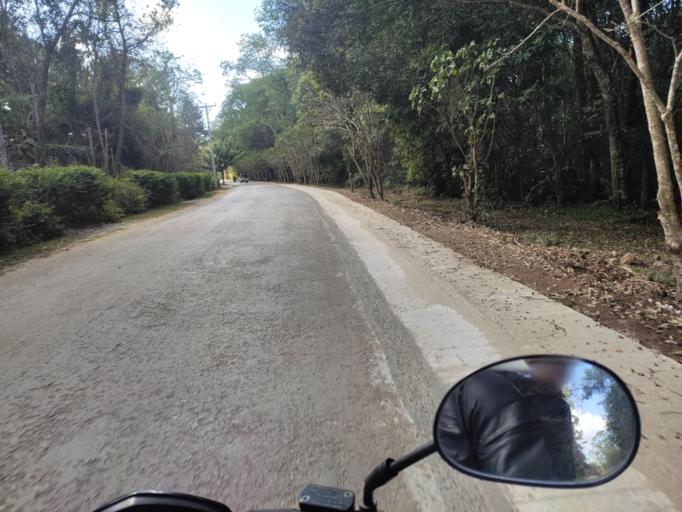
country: MM
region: Mandalay
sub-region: Pyin Oo Lwin District
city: Pyin Oo Lwin
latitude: 21.9897
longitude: 96.4709
